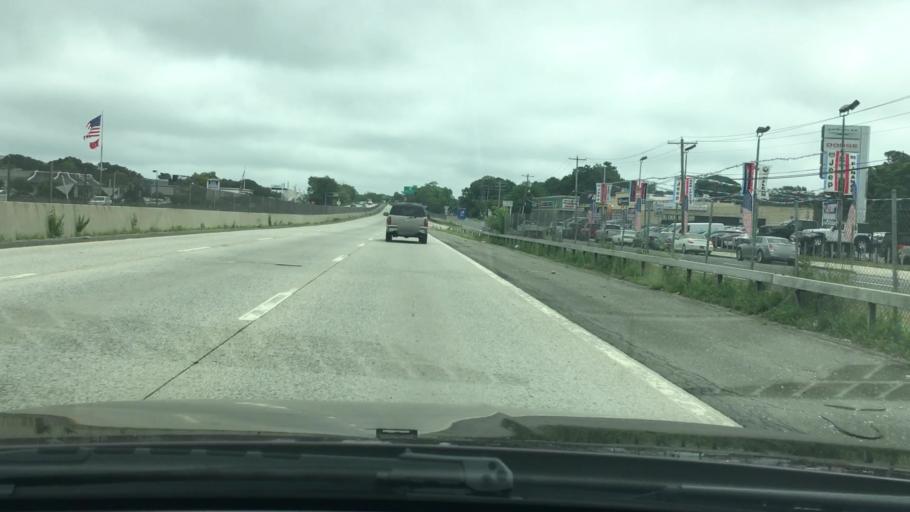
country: US
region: New York
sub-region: Suffolk County
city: North Babylon
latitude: 40.7186
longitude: -73.3096
